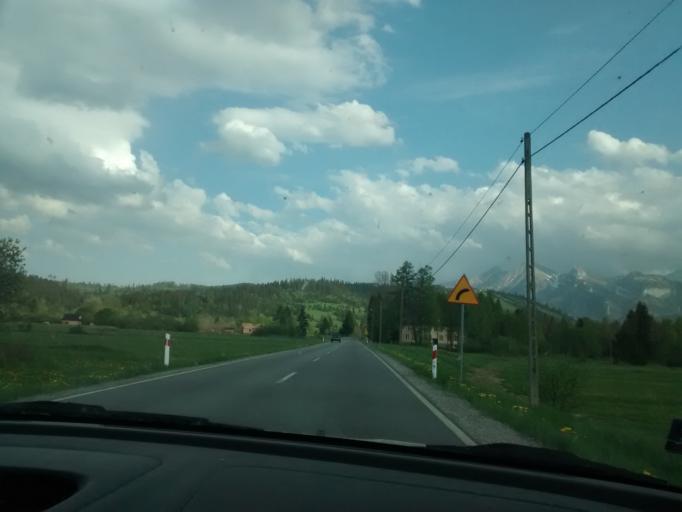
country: PL
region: Lesser Poland Voivodeship
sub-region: Powiat tatrzanski
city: Bukowina Tatrzanska
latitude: 49.3310
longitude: 20.1493
